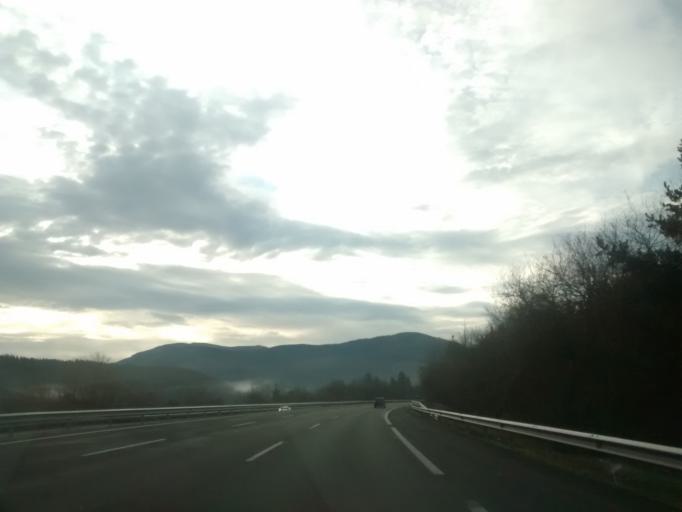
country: ES
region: Basque Country
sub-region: Bizkaia
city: Elexalde
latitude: 43.1225
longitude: -2.9171
